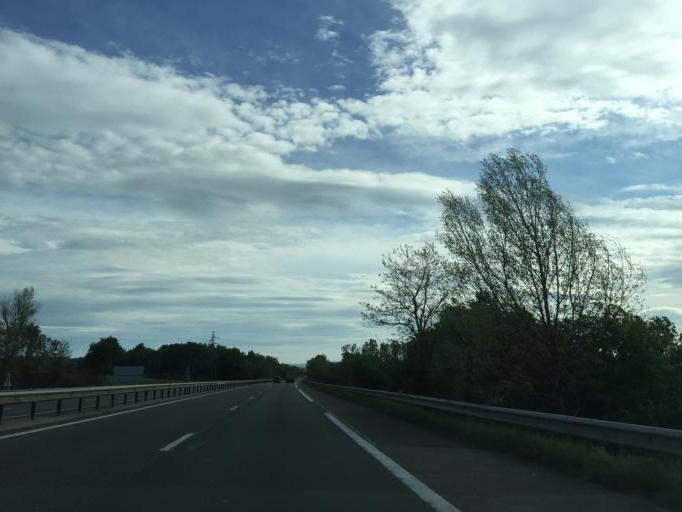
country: FR
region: Rhone-Alpes
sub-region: Departement de la Loire
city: Feurs
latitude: 45.7021
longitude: 4.1620
